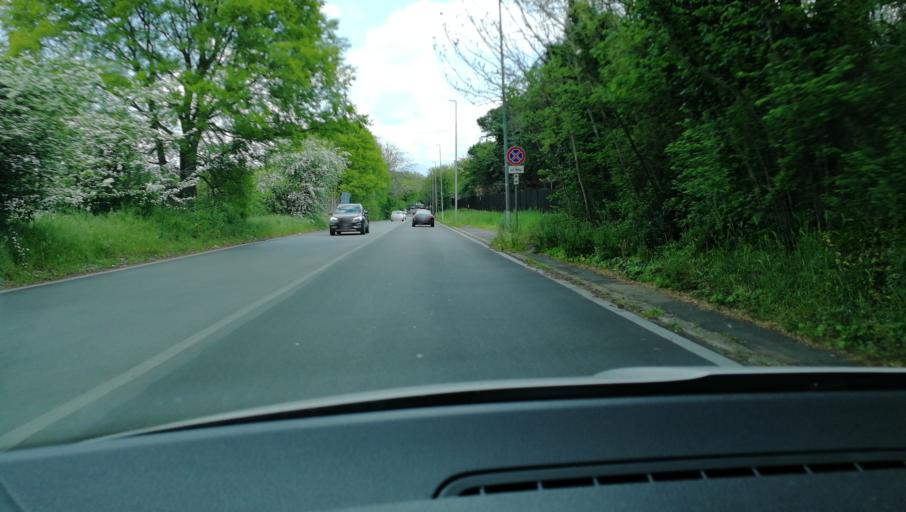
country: IT
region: Latium
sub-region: Citta metropolitana di Roma Capitale
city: Rome
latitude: 41.8530
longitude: 12.5277
